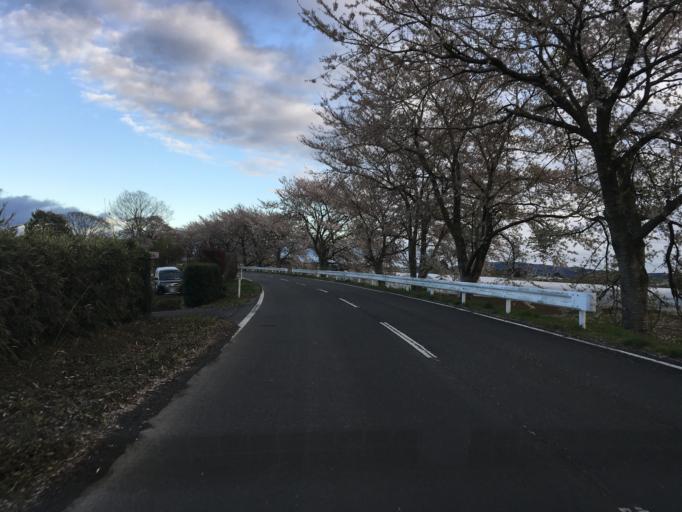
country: JP
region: Miyagi
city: Wakuya
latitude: 38.6462
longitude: 141.1461
